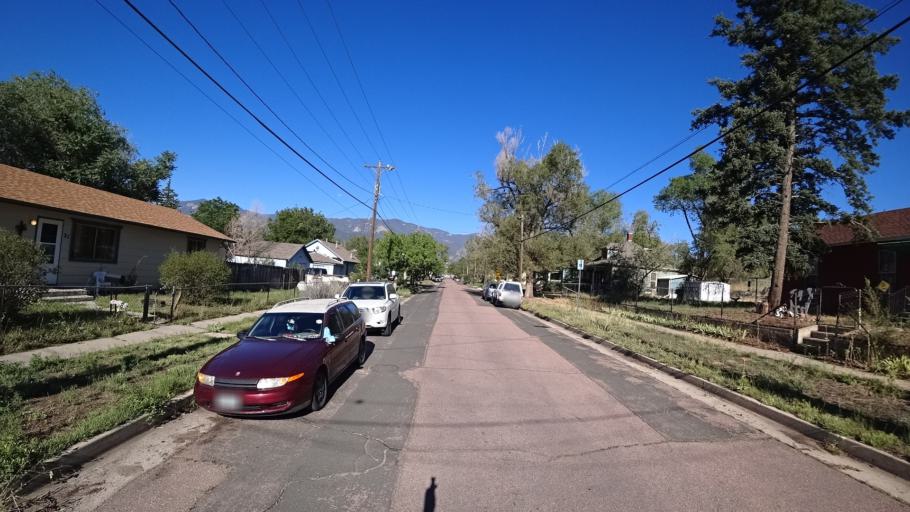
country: US
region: Colorado
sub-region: El Paso County
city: Colorado Springs
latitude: 38.8200
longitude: -104.8271
